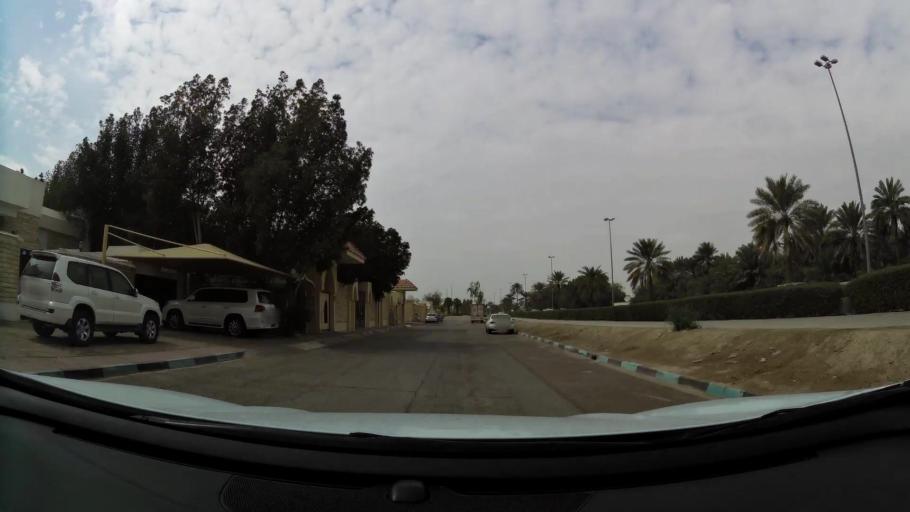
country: OM
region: Al Buraimi
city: Al Buraymi
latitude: 24.2291
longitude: 55.7818
